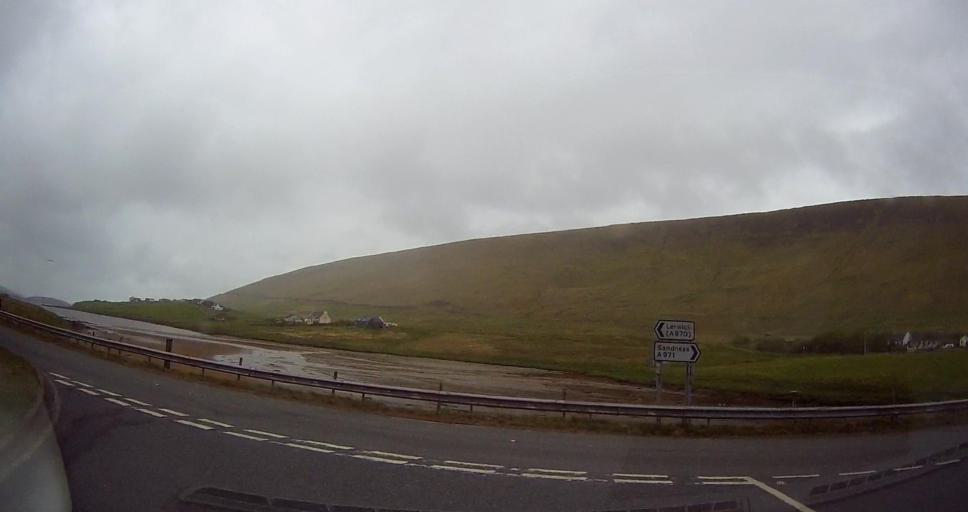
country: GB
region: Scotland
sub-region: Shetland Islands
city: Lerwick
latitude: 60.2536
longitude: -1.2914
